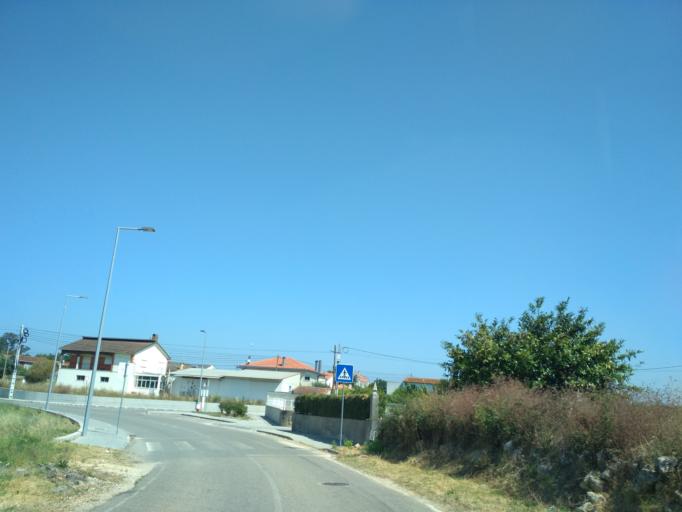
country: PT
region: Coimbra
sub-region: Soure
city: Soure
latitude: 40.0034
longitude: -8.5799
